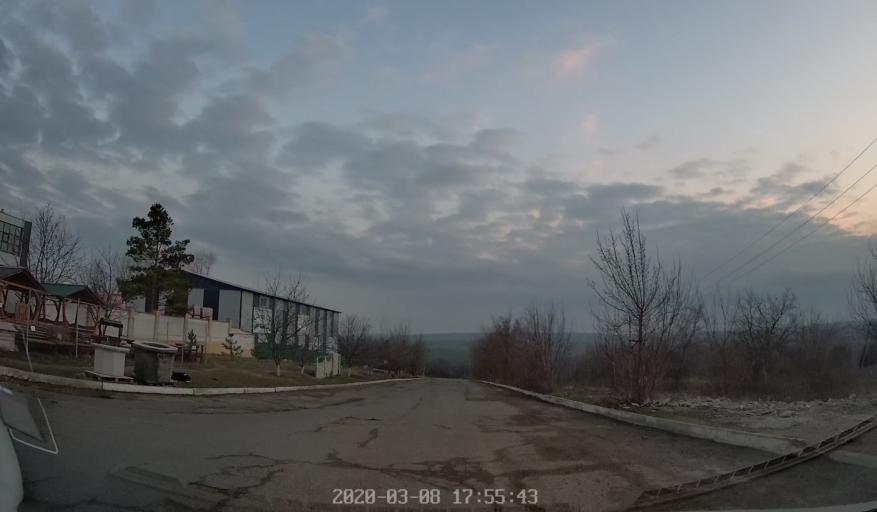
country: MD
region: Rezina
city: Rezina
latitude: 47.7505
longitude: 28.9490
